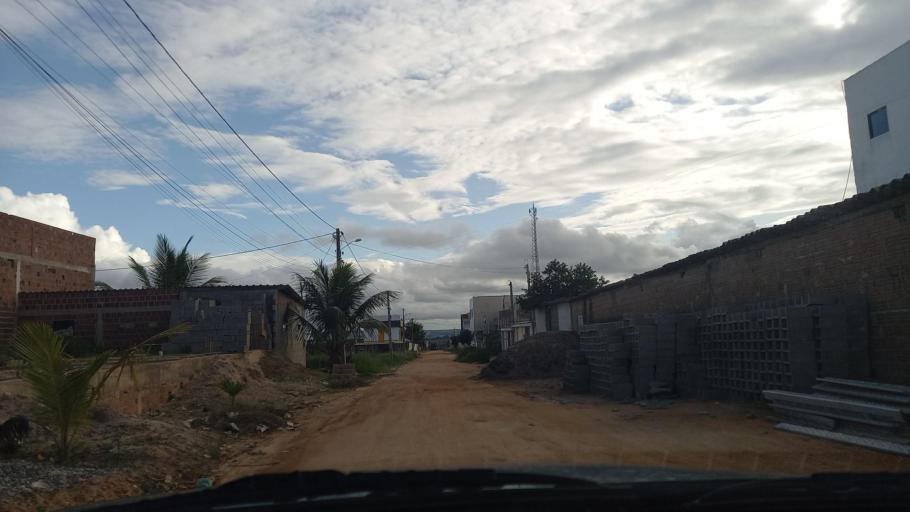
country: BR
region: Pernambuco
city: Garanhuns
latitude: -8.9139
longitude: -36.4780
